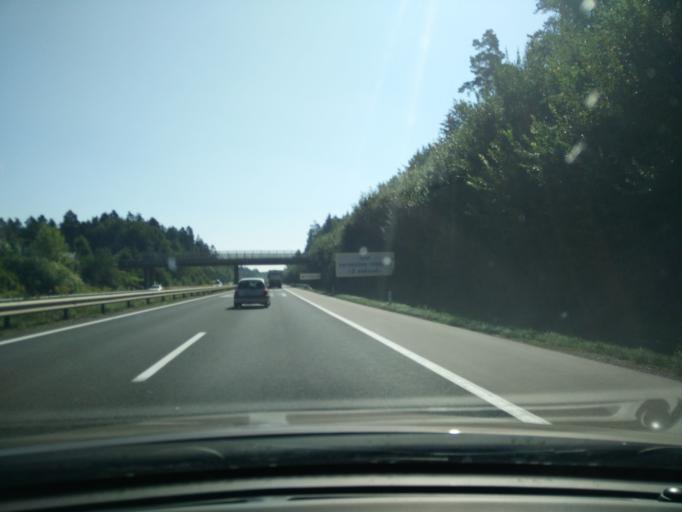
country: SI
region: Kranj
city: Kokrica
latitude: 46.2614
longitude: 14.3589
